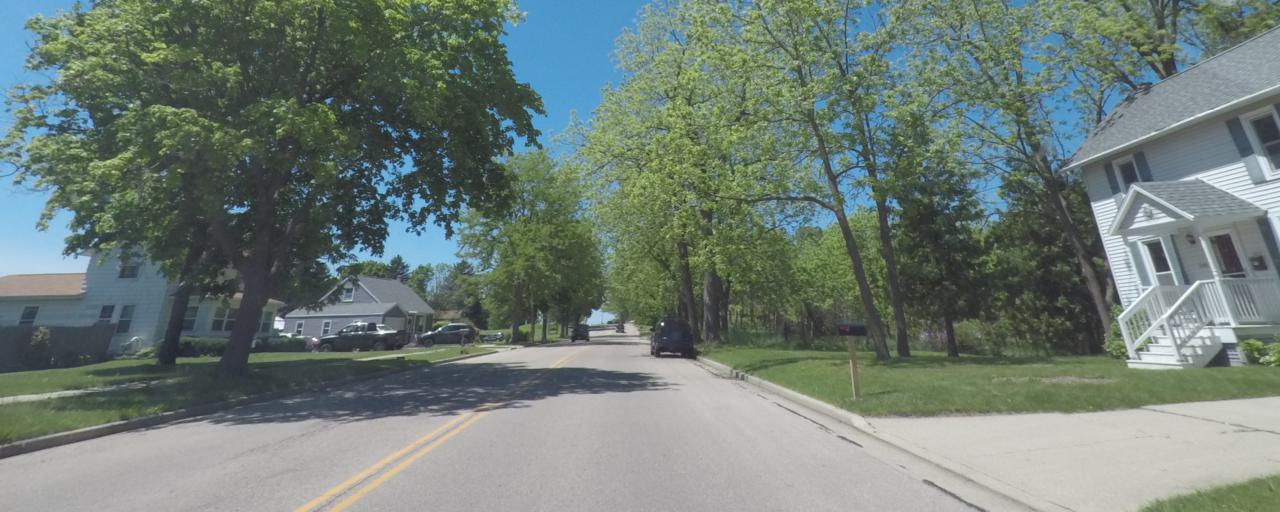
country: US
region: Wisconsin
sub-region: Rock County
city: Evansville
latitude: 42.7836
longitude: -89.3113
